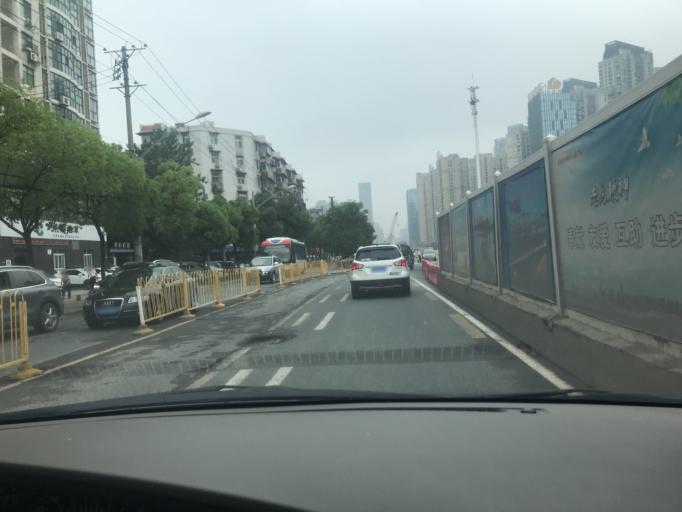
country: CN
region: Hubei
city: Jiang'an
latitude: 30.5873
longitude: 114.3231
